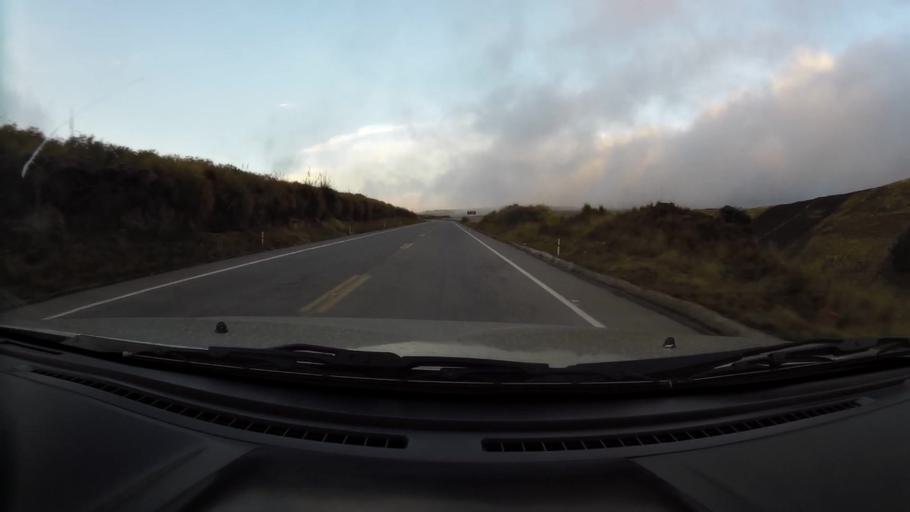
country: EC
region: Chimborazo
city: Alausi
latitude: -2.1299
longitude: -78.7561
